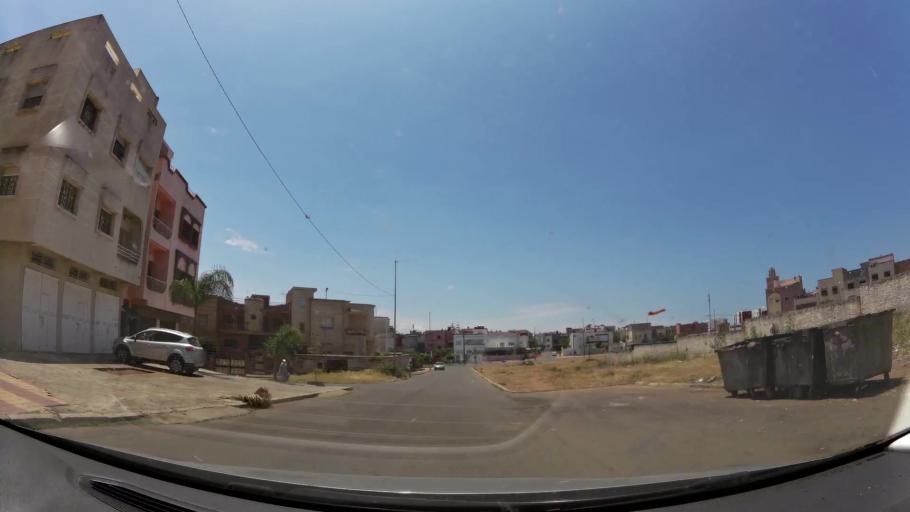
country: MA
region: Gharb-Chrarda-Beni Hssen
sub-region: Kenitra Province
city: Kenitra
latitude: 34.2666
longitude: -6.6211
